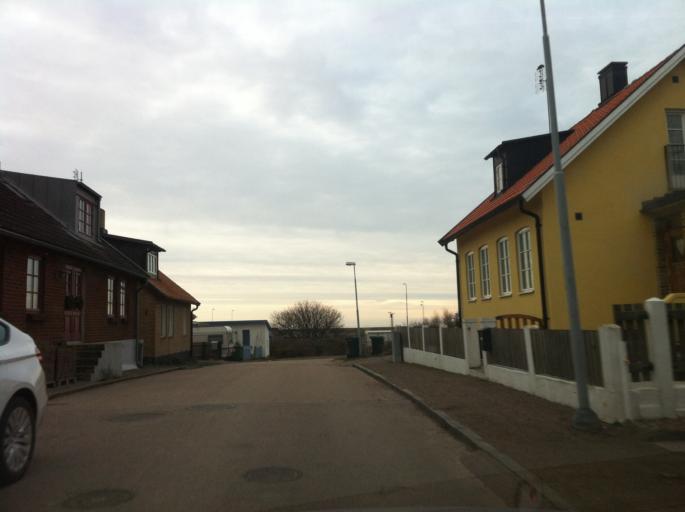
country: SE
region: Skane
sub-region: Hoganas Kommun
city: Hoganas
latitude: 56.2016
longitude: 12.5465
